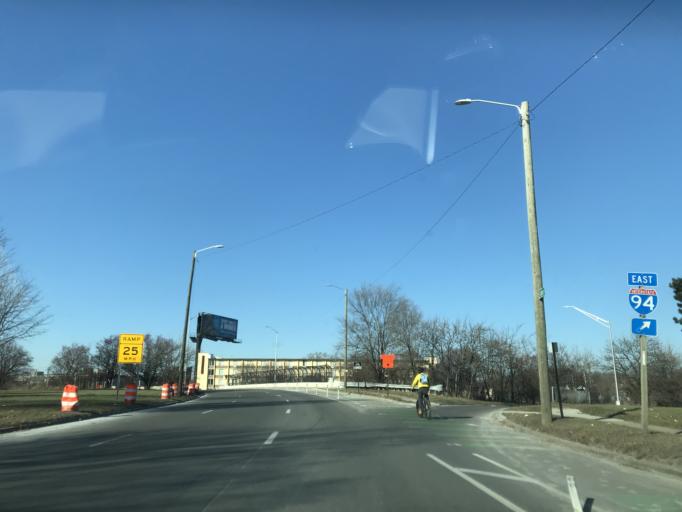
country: US
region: Michigan
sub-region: Wayne County
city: Grosse Pointe Park
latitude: 42.3960
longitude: -82.9868
